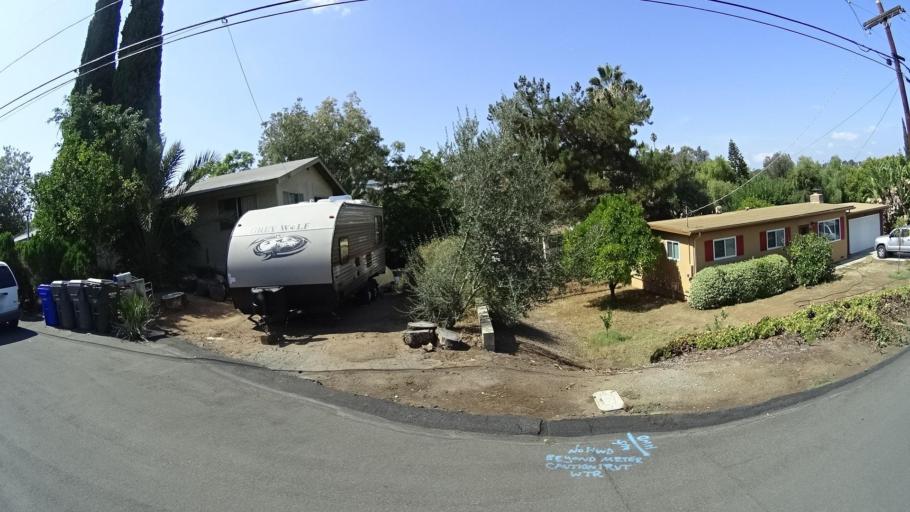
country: US
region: California
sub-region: San Diego County
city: Spring Valley
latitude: 32.7425
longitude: -116.9804
